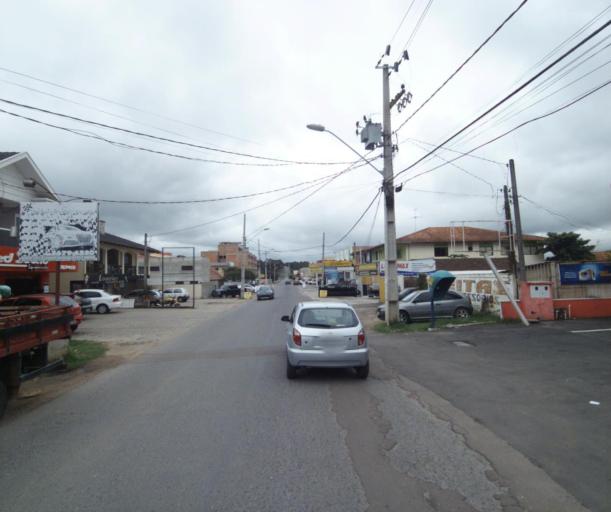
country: BR
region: Parana
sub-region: Quatro Barras
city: Quatro Barras
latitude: -25.3635
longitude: -49.0975
